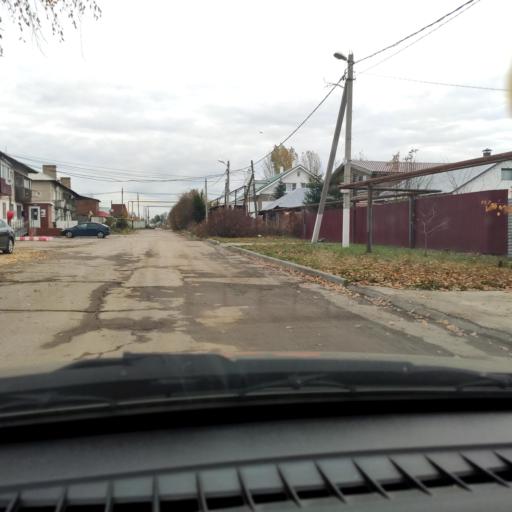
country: RU
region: Samara
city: Podstepki
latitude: 53.5112
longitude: 49.2309
